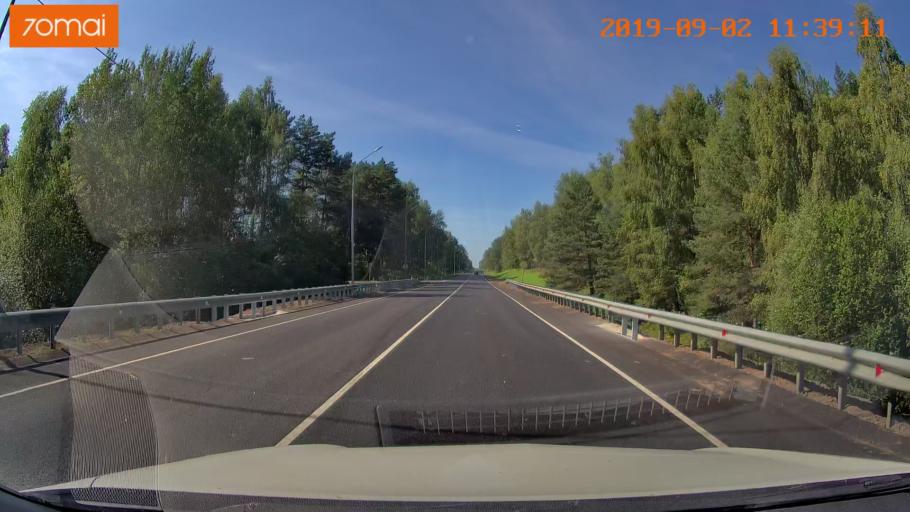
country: RU
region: Smolensk
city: Oster
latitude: 53.9094
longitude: 32.7277
